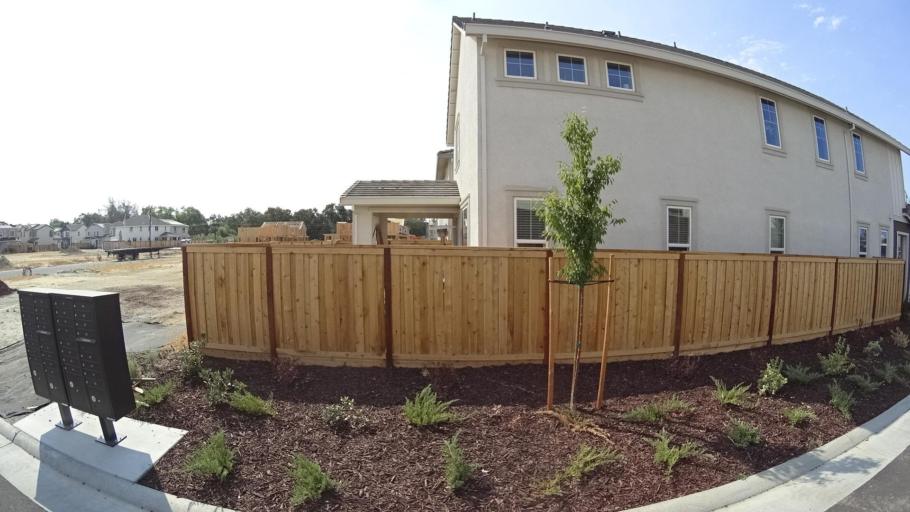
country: US
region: California
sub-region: Placer County
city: Rocklin
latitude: 38.8008
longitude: -121.2200
